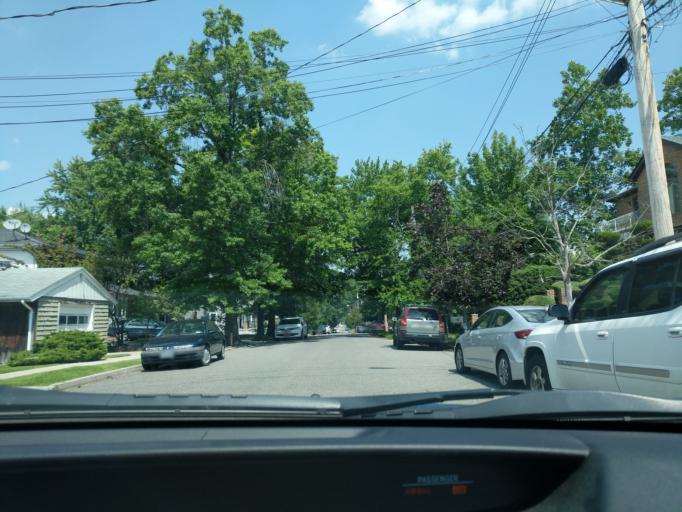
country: US
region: New York
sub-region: Richmond County
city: Staten Island
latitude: 40.5388
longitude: -74.1770
